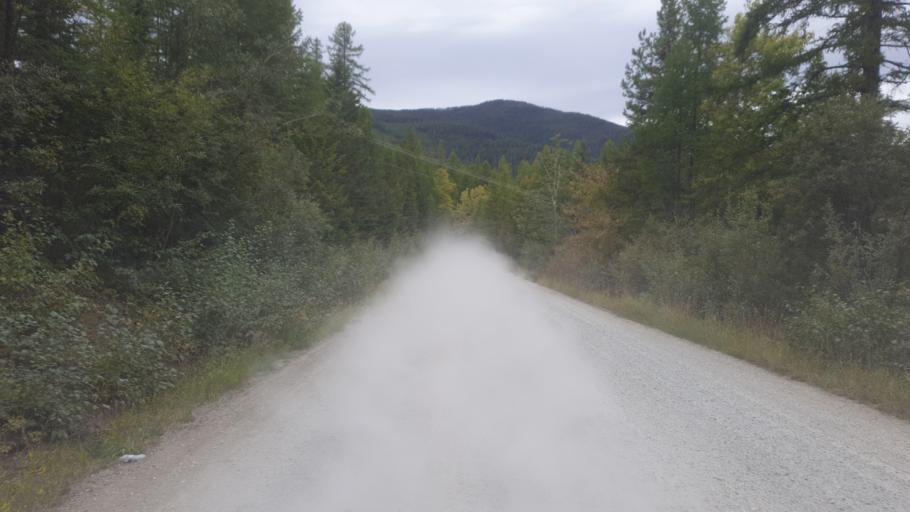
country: US
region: Montana
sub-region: Flathead County
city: Lakeside
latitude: 47.9910
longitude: -114.3254
